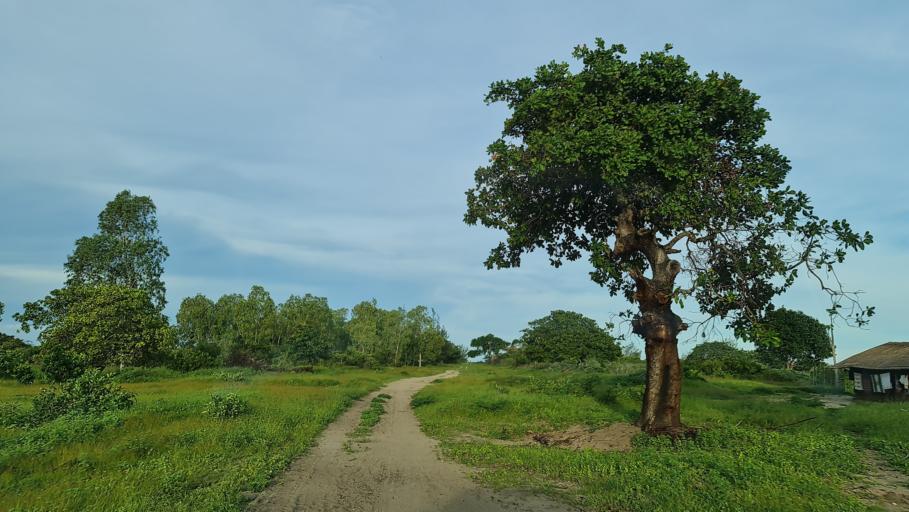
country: MZ
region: Nampula
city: Nacala
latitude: -14.7782
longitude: 40.8193
